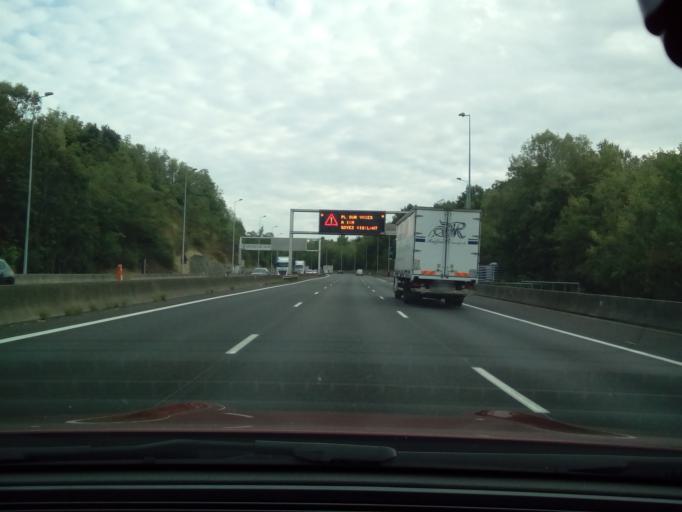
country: FR
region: Rhone-Alpes
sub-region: Departement du Rhone
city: Rillieux-la-Pape
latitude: 45.8148
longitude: 4.9168
